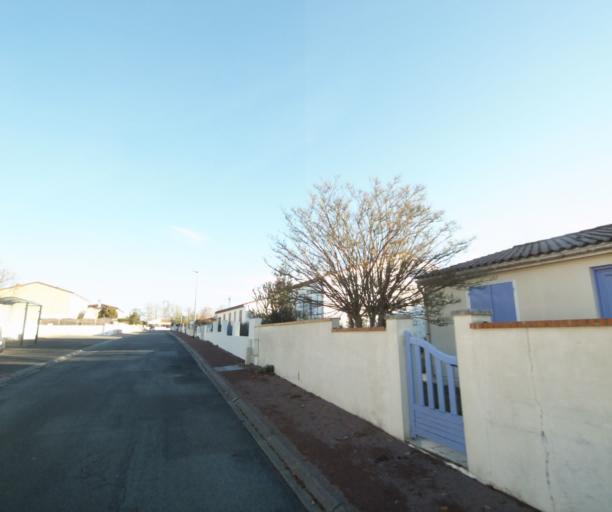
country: FR
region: Poitou-Charentes
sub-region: Departement de la Charente-Maritime
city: Saintes
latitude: 45.7643
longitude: -0.6137
